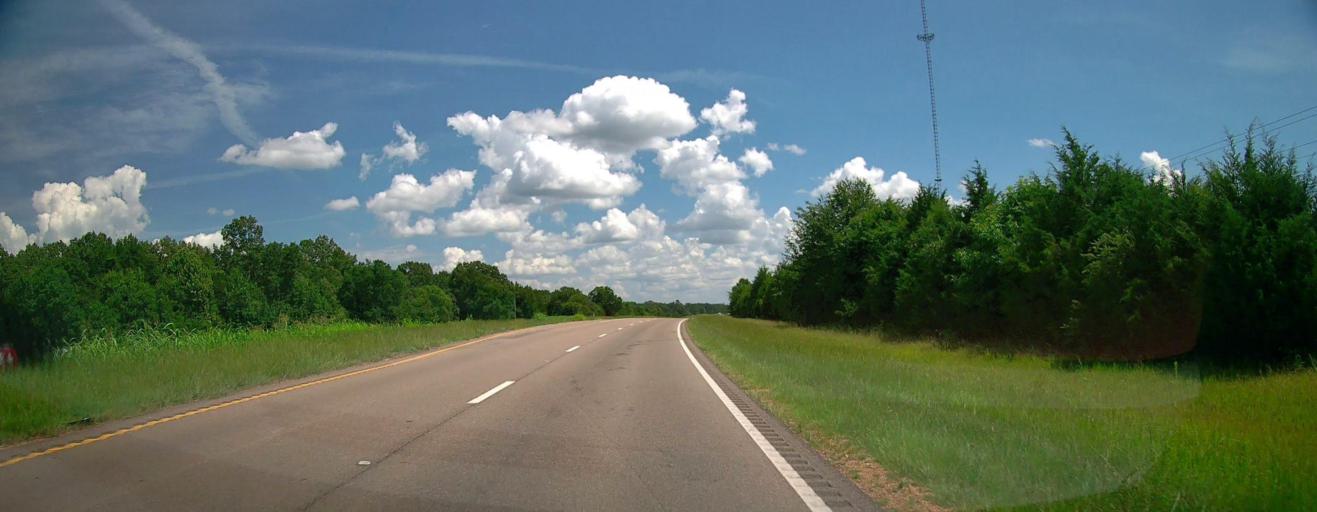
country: US
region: Mississippi
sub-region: Monroe County
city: Amory
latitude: 33.9531
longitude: -88.6047
